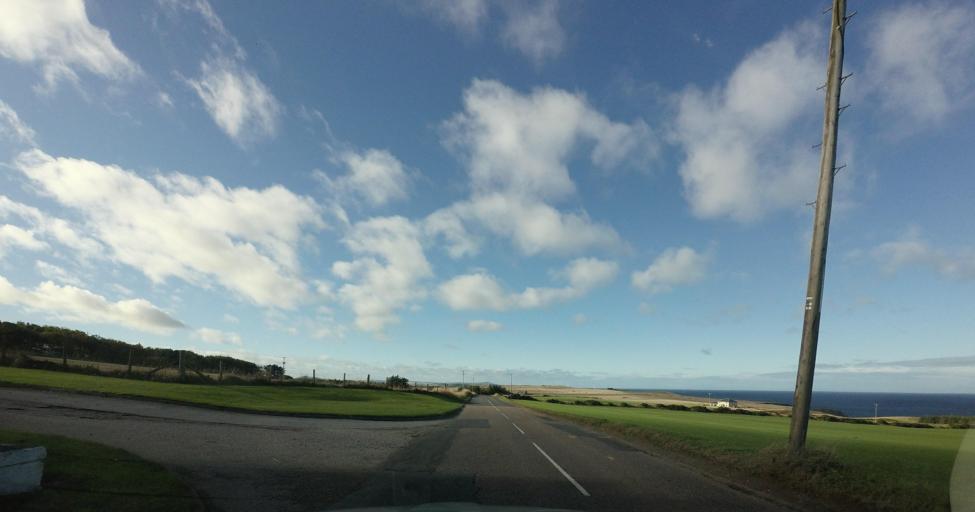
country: GB
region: Scotland
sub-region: Aberdeenshire
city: Macduff
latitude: 57.6629
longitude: -2.4368
